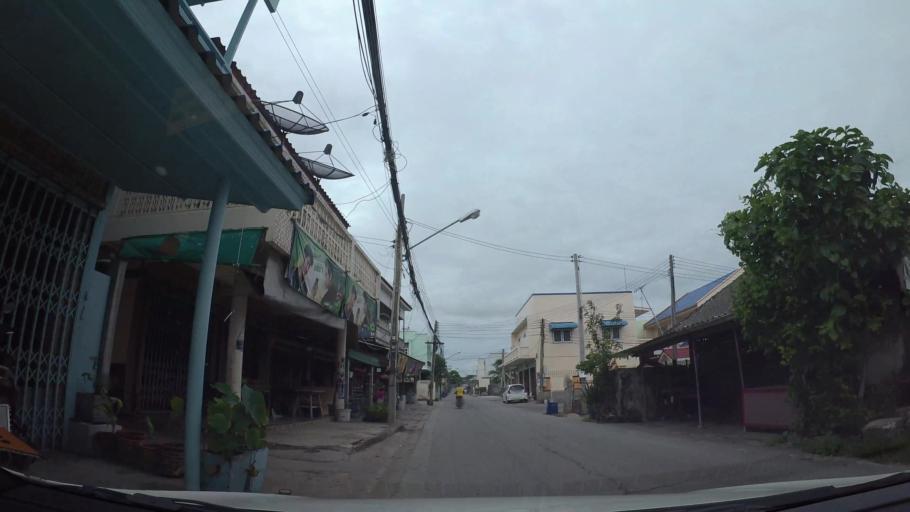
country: TH
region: Rayong
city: Rayong
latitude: 12.6609
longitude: 101.2723
